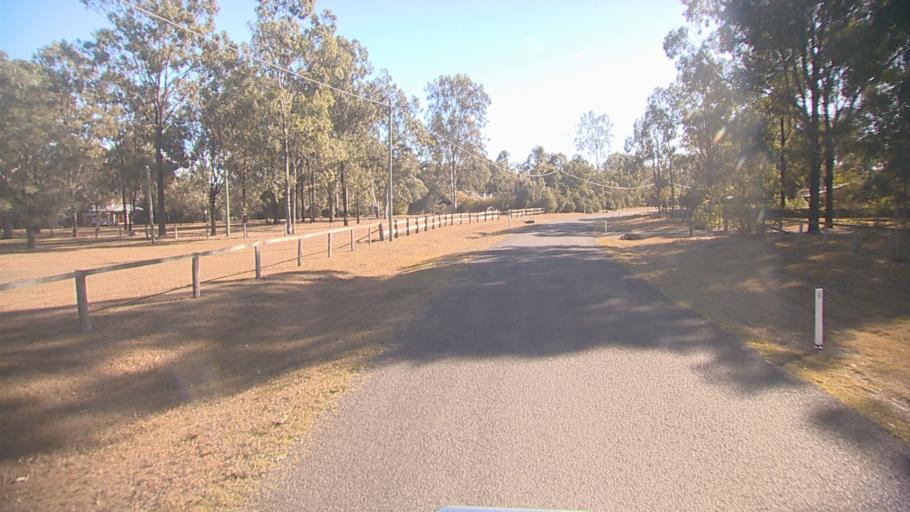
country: AU
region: Queensland
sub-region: Logan
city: North Maclean
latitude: -27.8289
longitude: 152.9901
